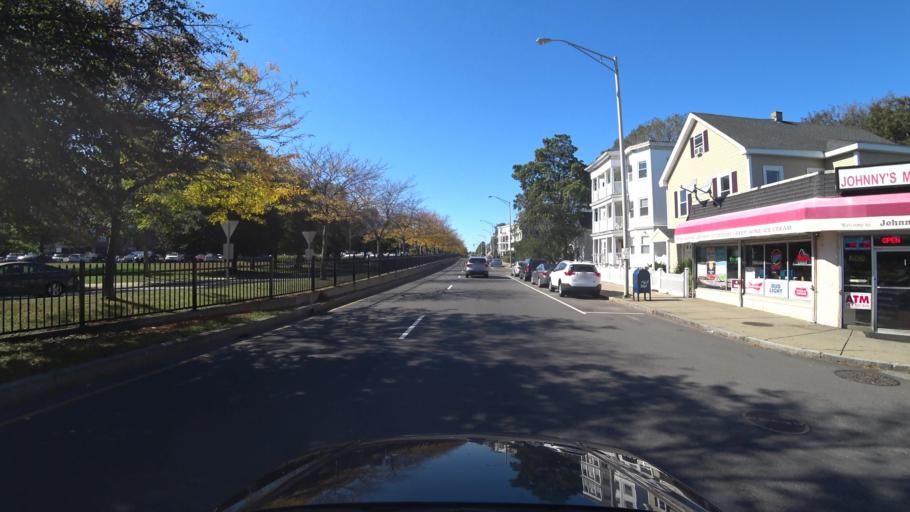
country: US
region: Massachusetts
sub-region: Essex County
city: Lynn
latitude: 42.4576
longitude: -70.9373
